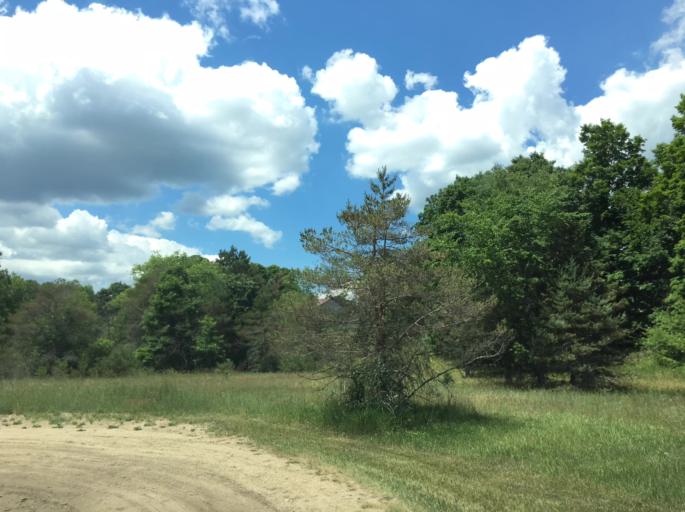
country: US
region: Michigan
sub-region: Osceola County
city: Evart
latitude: 43.8611
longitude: -85.3784
